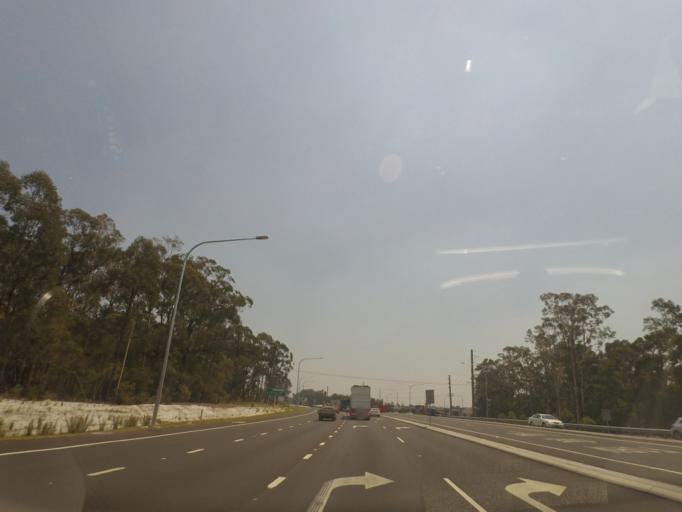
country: AU
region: New South Wales
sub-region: Newcastle
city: Beresfield
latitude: -32.8154
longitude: 151.6357
